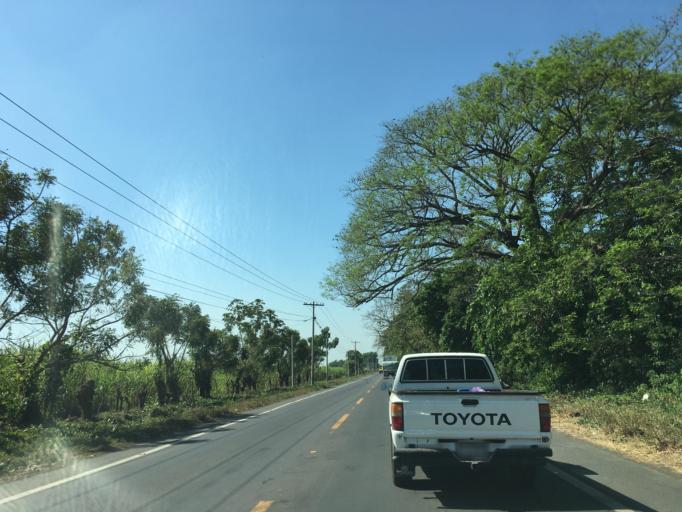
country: GT
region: Escuintla
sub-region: Municipio de Masagua
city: Masagua
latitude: 14.1956
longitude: -90.8545
